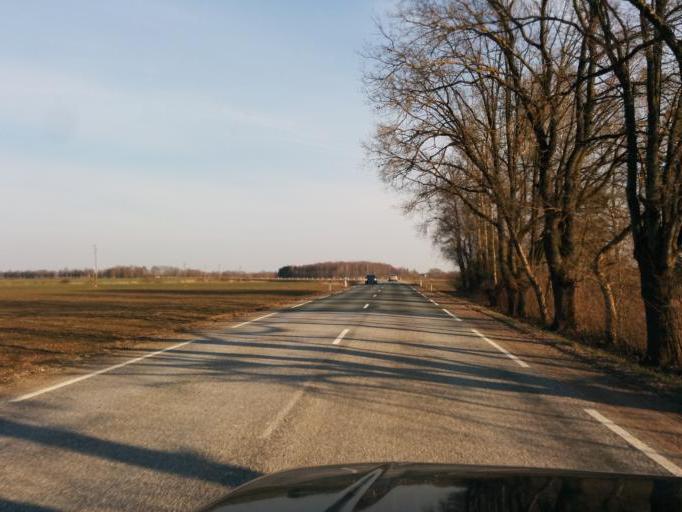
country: LV
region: Lecava
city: Iecava
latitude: 56.5915
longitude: 24.1334
